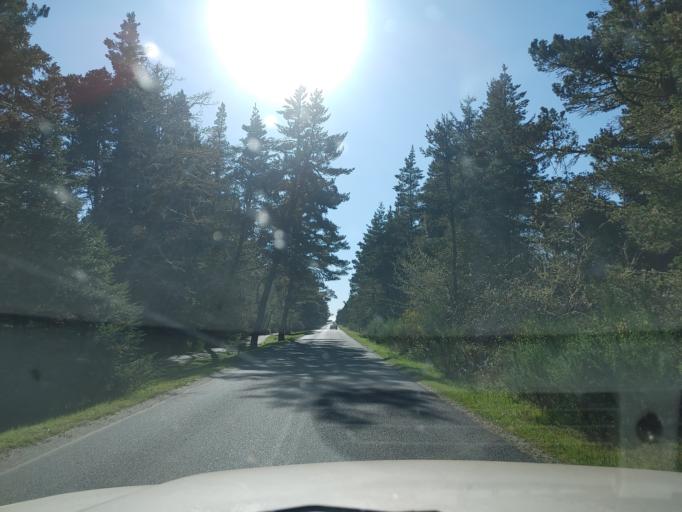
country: US
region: Oregon
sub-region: Clatsop County
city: Warrenton
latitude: 46.1797
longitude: -123.9719
